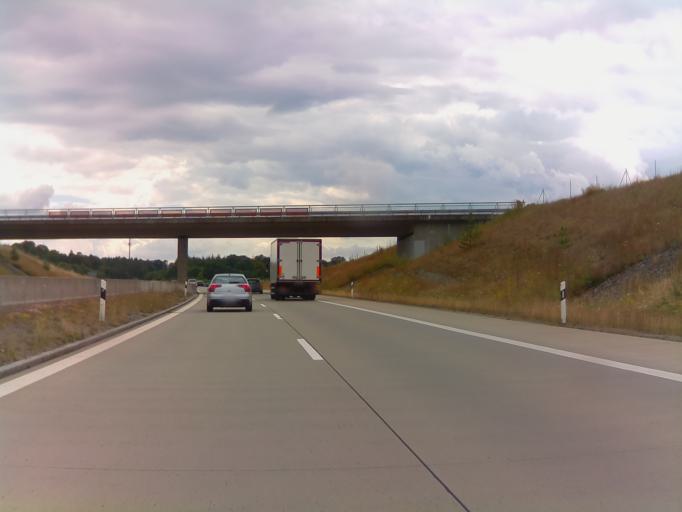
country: DE
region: Bavaria
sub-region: Regierungsbezirk Unterfranken
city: Rodelmaier
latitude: 50.3086
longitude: 10.2822
